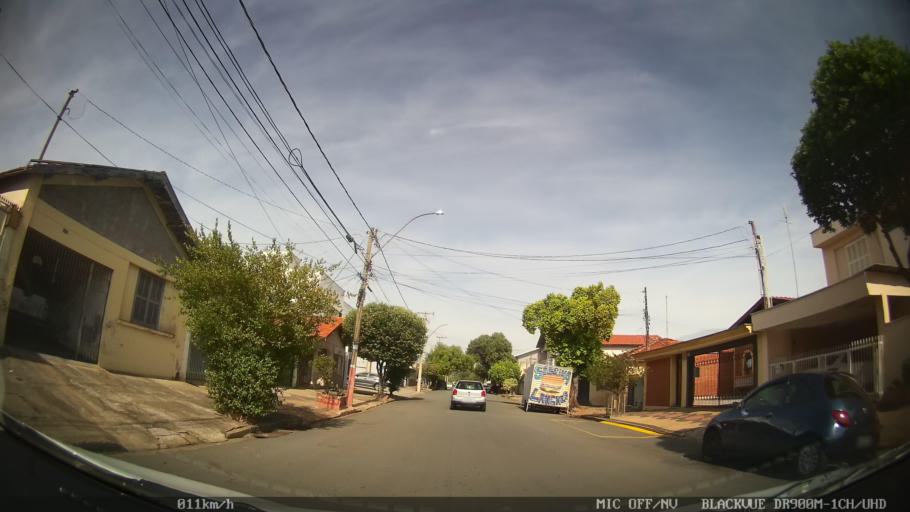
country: BR
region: Sao Paulo
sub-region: Piracicaba
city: Piracicaba
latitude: -22.7102
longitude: -47.6591
